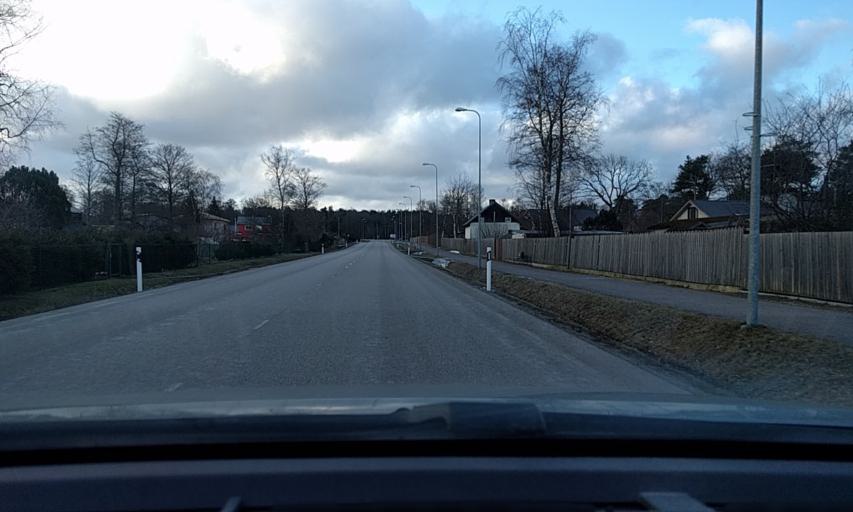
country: EE
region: Harju
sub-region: Viimsi vald
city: Viimsi
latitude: 59.5019
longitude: 24.9042
